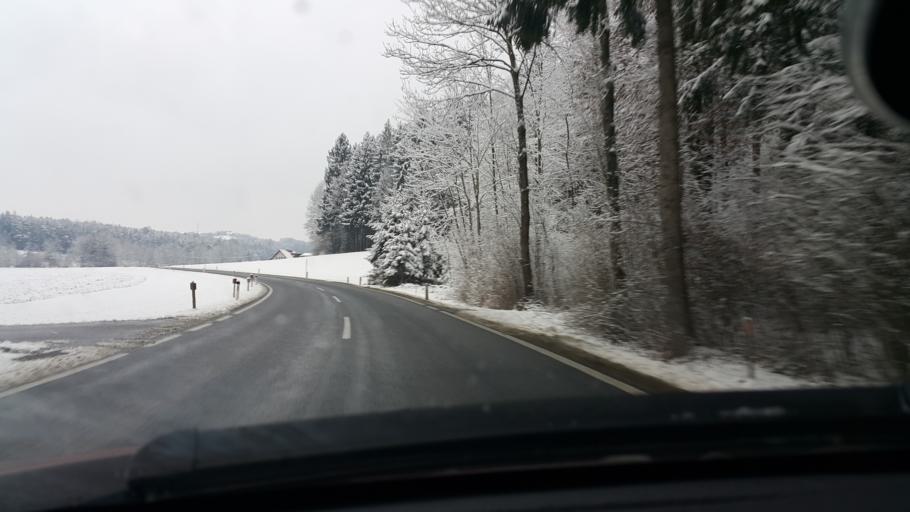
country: AT
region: Styria
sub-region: Politischer Bezirk Graz-Umgebung
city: Hitzendorf
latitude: 47.0499
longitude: 15.2930
